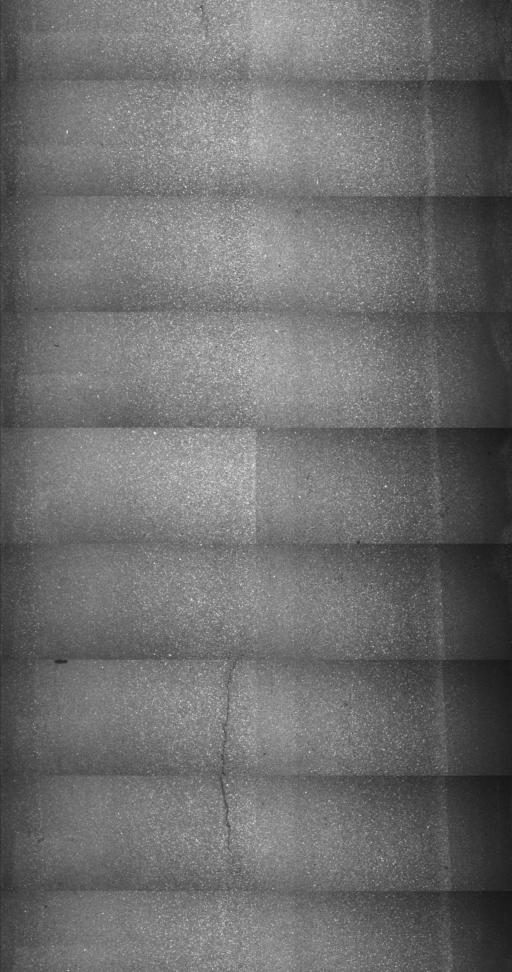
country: US
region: Vermont
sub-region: Franklin County
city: Richford
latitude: 44.9324
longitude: -72.4936
